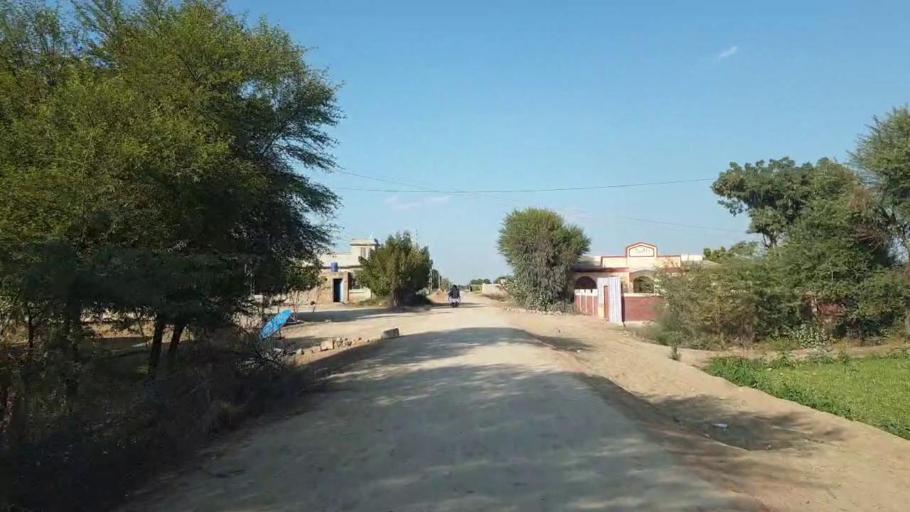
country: PK
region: Sindh
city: Shahpur Chakar
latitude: 26.1049
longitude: 68.5927
